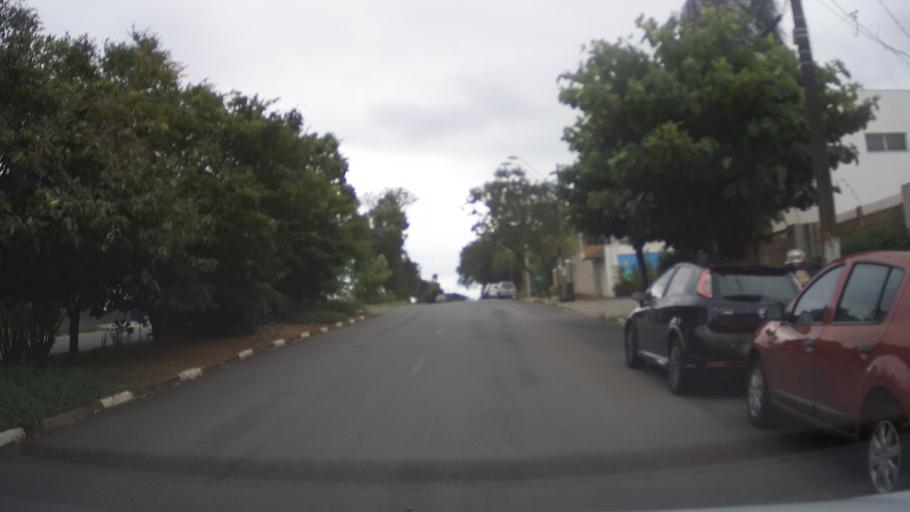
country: BR
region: Sao Paulo
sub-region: Campinas
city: Campinas
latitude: -22.9088
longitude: -47.0355
